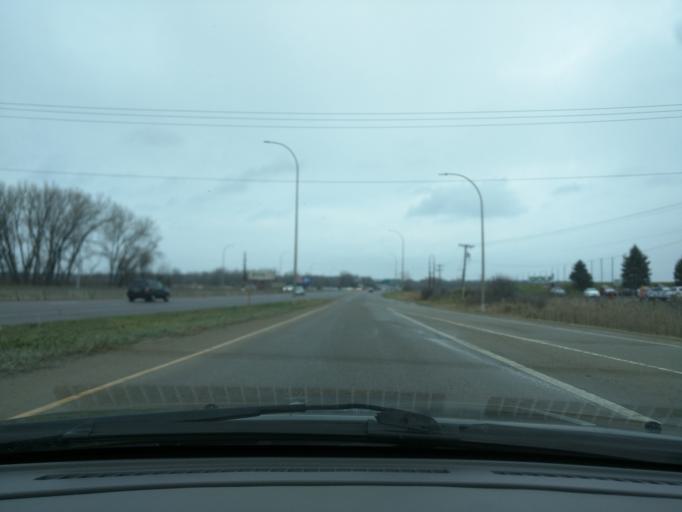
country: US
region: Minnesota
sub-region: Dakota County
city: Burnsville
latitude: 44.7859
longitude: -93.2883
